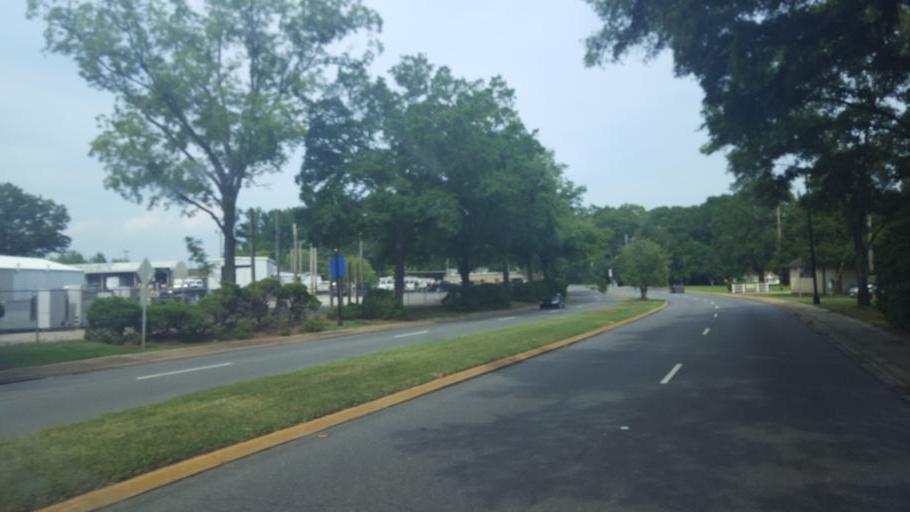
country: US
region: South Carolina
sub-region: York County
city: Rock Hill
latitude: 34.9299
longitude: -81.0202
